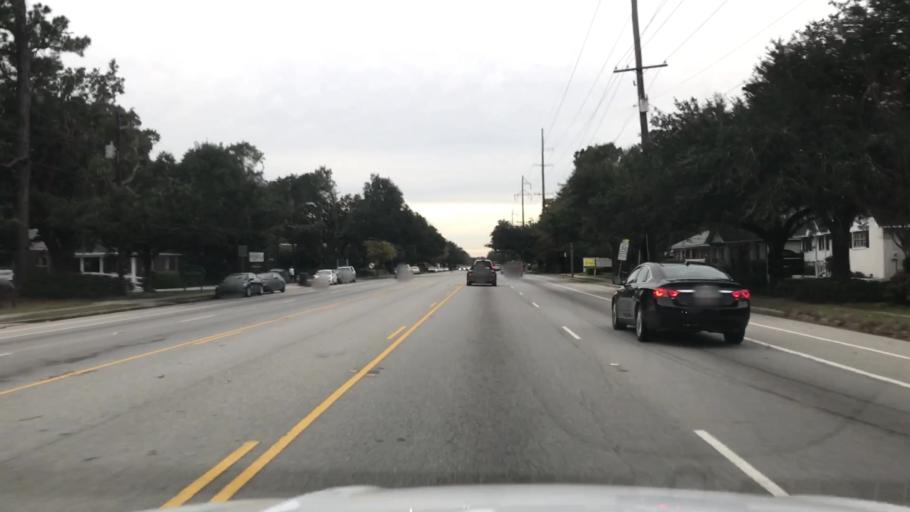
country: US
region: South Carolina
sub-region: Charleston County
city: Charleston
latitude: 32.7871
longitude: -79.9815
